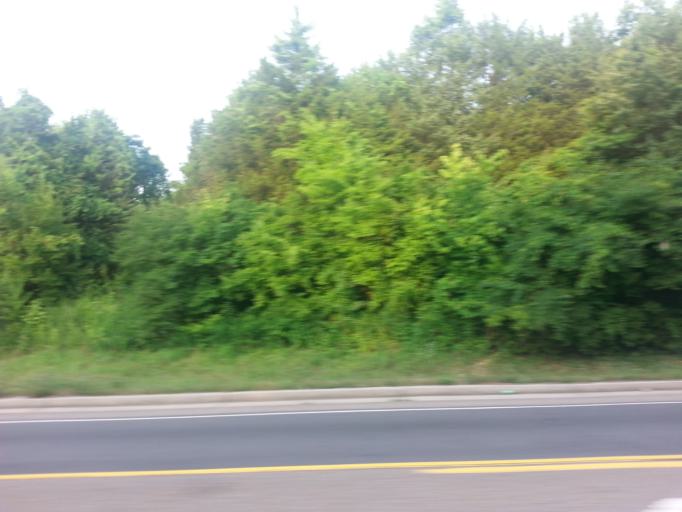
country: US
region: Tennessee
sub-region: Knox County
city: Mascot
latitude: 36.0098
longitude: -83.8250
